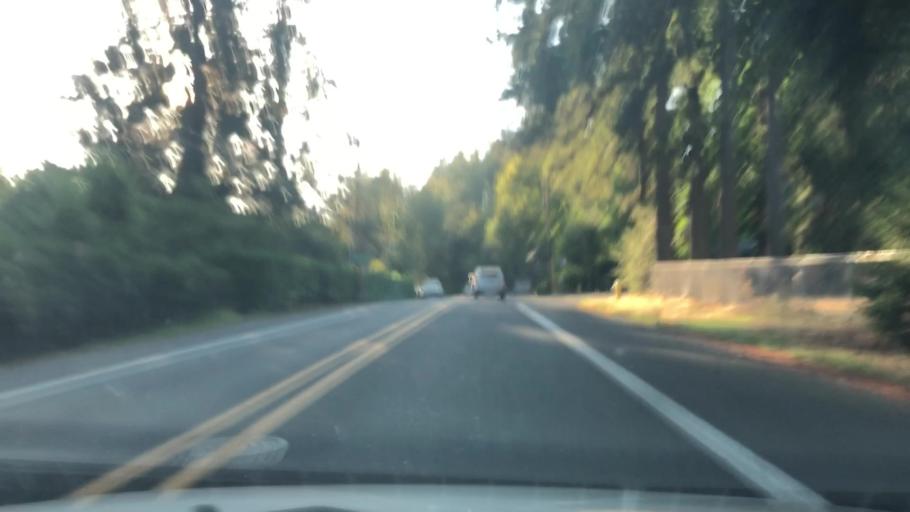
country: US
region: Oregon
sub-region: Clackamas County
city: Oak Grove
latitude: 45.4061
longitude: -122.6413
